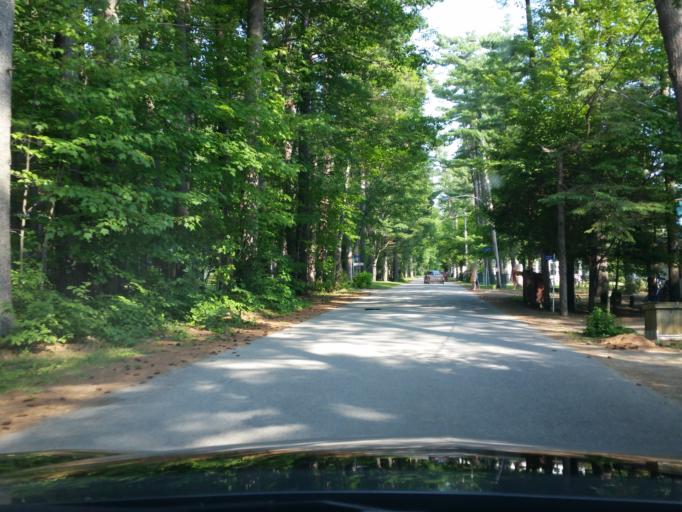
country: CA
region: Ontario
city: Arnprior
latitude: 45.5160
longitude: -76.4137
